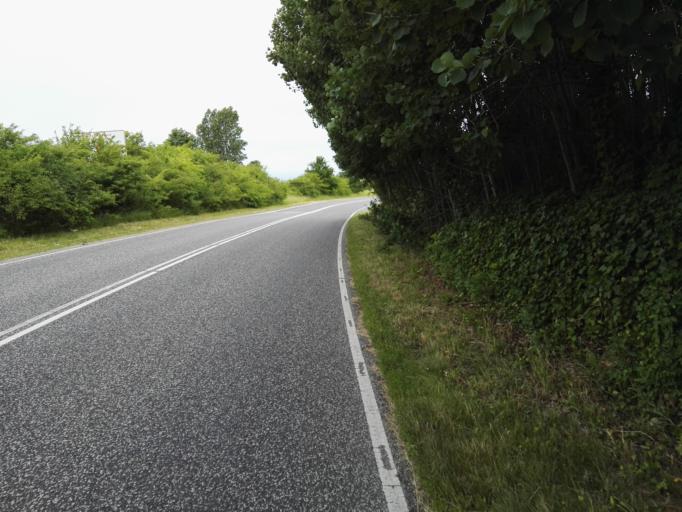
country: DK
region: Zealand
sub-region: Roskilde Kommune
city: Jyllinge
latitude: 55.7847
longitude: 12.1205
